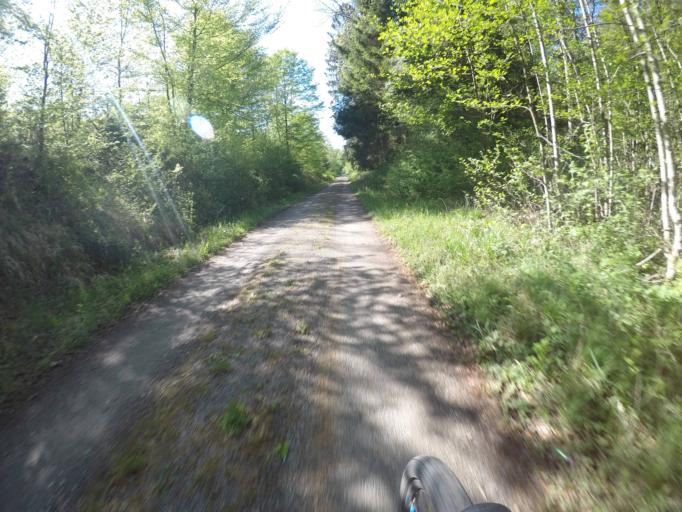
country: DE
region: Baden-Wuerttemberg
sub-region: Tuebingen Region
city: Dettenhausen
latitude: 48.5781
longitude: 9.0931
